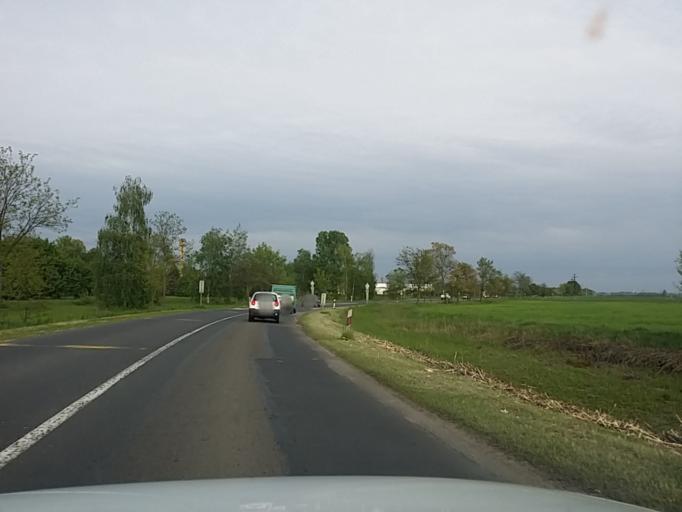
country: HU
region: Jasz-Nagykun-Szolnok
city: Jaszbereny
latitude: 47.5262
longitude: 19.8544
